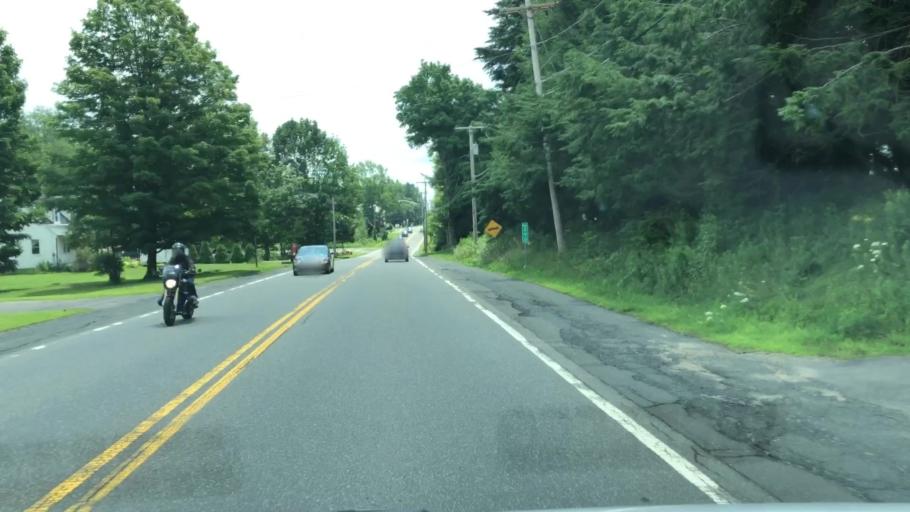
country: US
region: Massachusetts
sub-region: Hampshire County
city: Chesterfield
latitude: 42.4443
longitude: -72.8014
